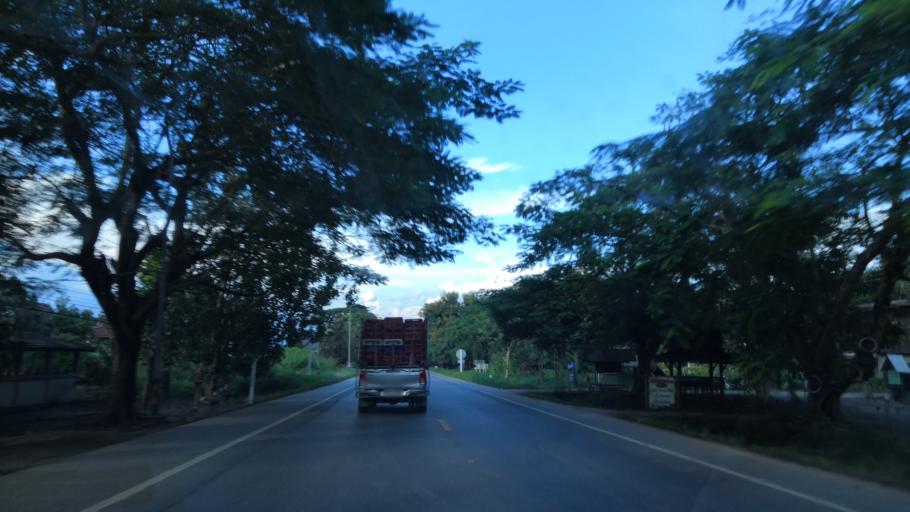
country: TH
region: Chiang Rai
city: Mae Suai
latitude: 19.5443
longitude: 99.4921
